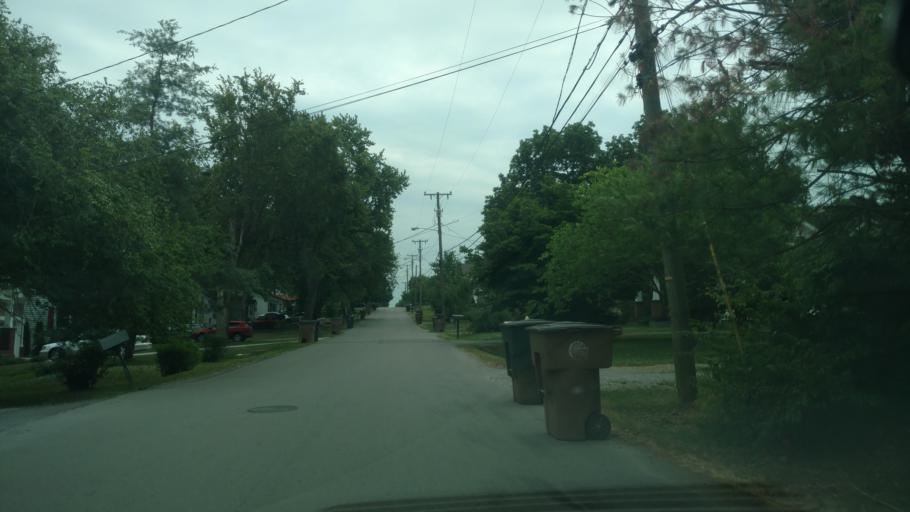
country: US
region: Tennessee
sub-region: Davidson County
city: Nashville
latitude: 36.2017
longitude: -86.7218
